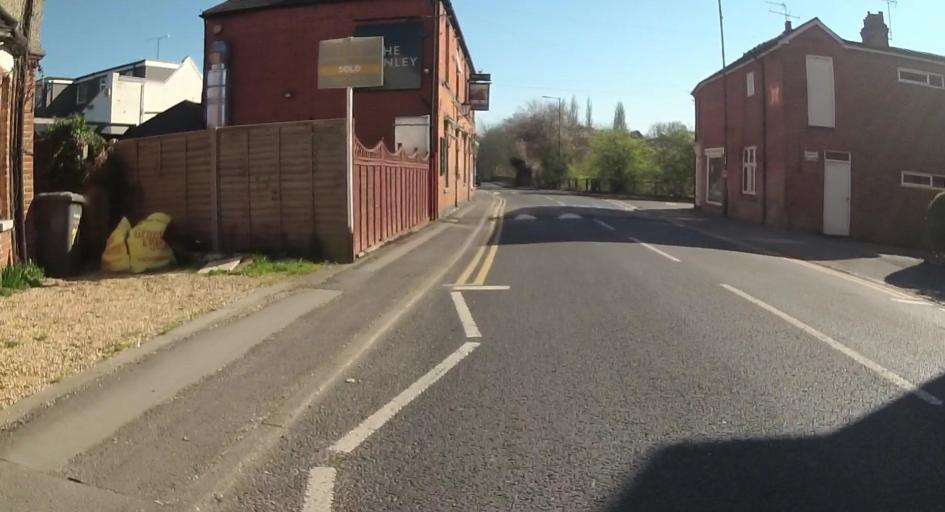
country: GB
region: England
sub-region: Royal Borough of Windsor and Maidenhead
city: Ascot
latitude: 51.4032
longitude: -0.6716
